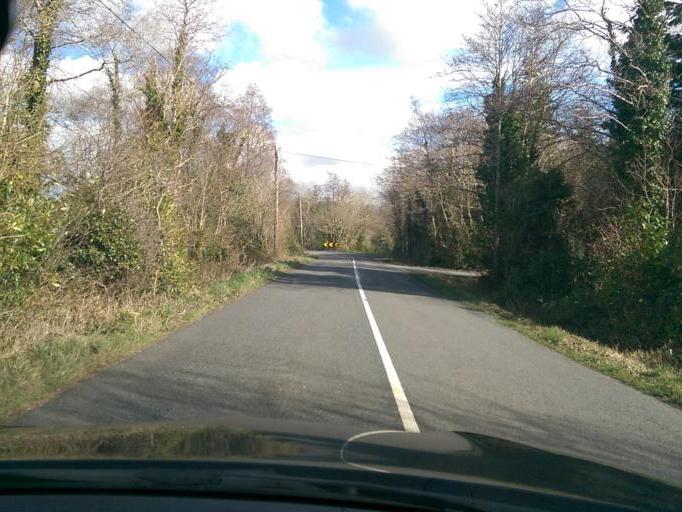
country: IE
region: Connaught
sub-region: County Galway
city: Loughrea
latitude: 53.4682
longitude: -8.5277
